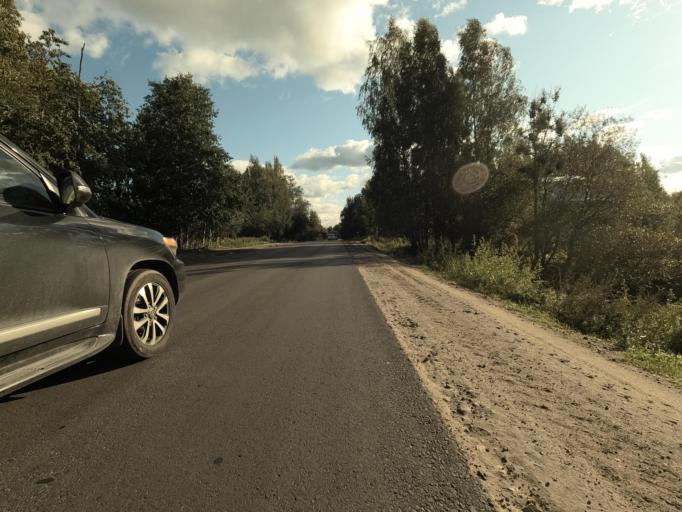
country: RU
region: Leningrad
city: Koltushi
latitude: 59.9283
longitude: 30.6641
